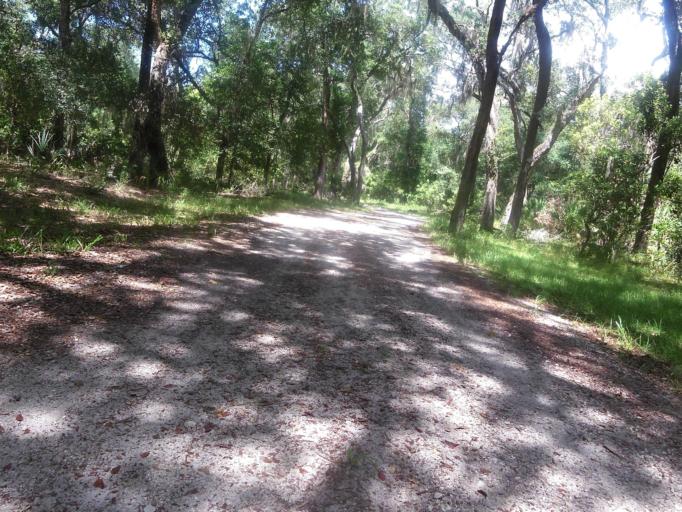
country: US
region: Florida
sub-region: Saint Johns County
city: Villano Beach
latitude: 30.0326
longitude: -81.3367
